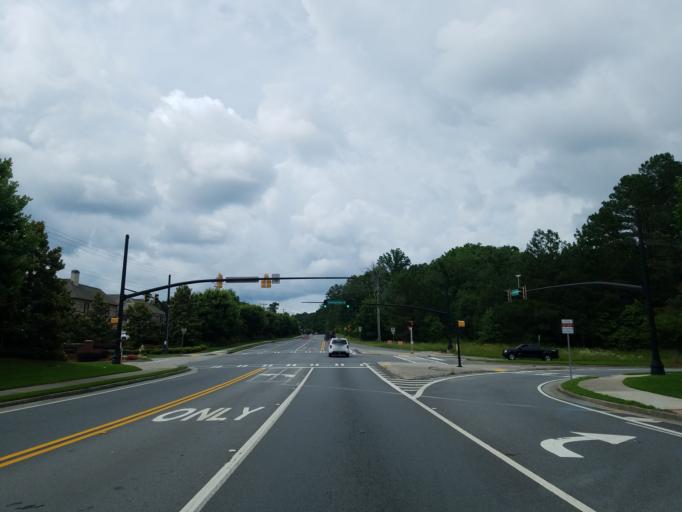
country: US
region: Georgia
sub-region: Fulton County
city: Alpharetta
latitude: 34.1061
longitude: -84.2695
